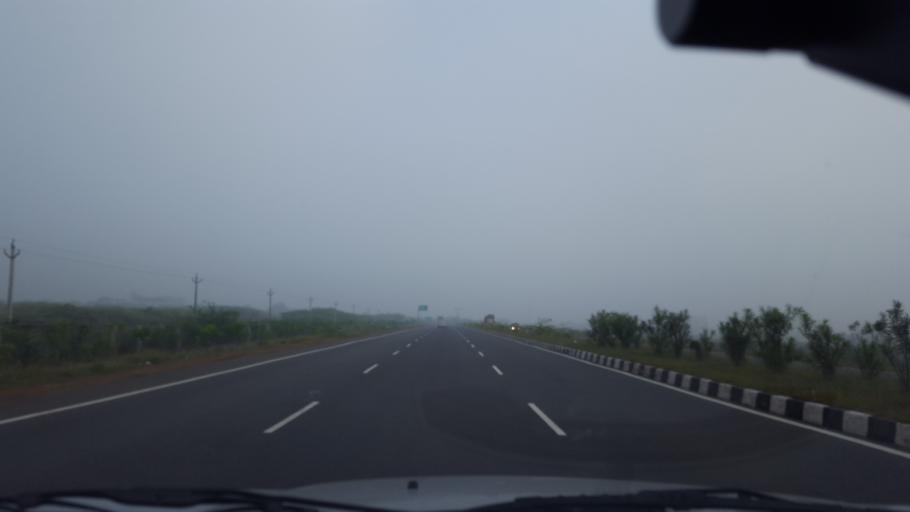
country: IN
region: Andhra Pradesh
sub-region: Prakasam
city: Ongole
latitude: 15.4893
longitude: 80.0647
